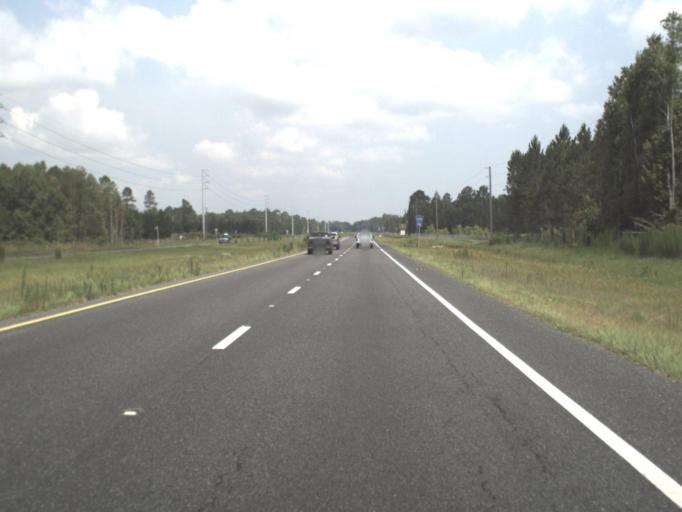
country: US
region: Florida
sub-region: Levy County
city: Bronson
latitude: 29.4669
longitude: -82.6692
